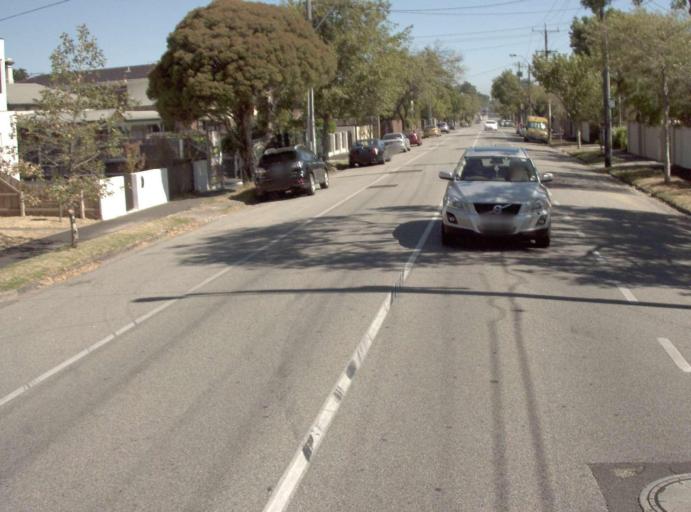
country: AU
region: Victoria
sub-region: Bayside
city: North Brighton
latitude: -37.9086
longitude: 145.0079
